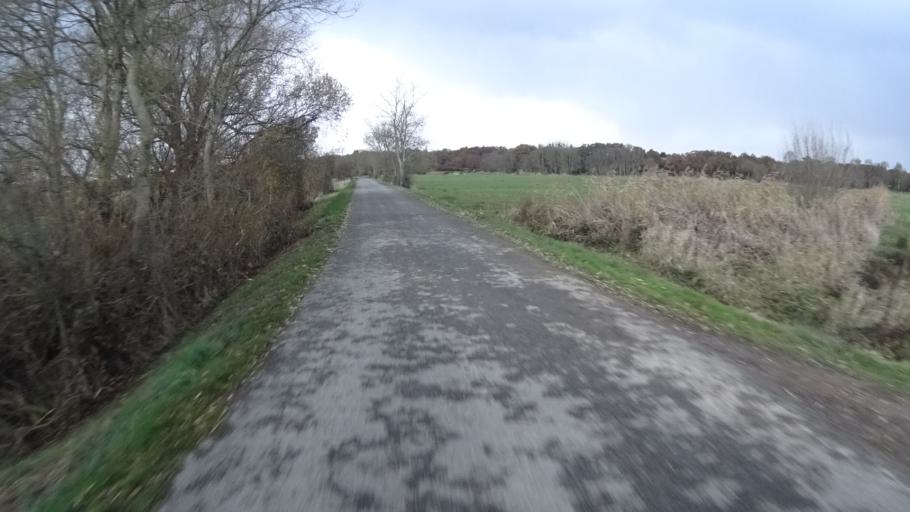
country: FR
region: Brittany
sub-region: Departement d'Ille-et-Vilaine
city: Sainte-Marie
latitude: 47.6689
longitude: -2.0299
